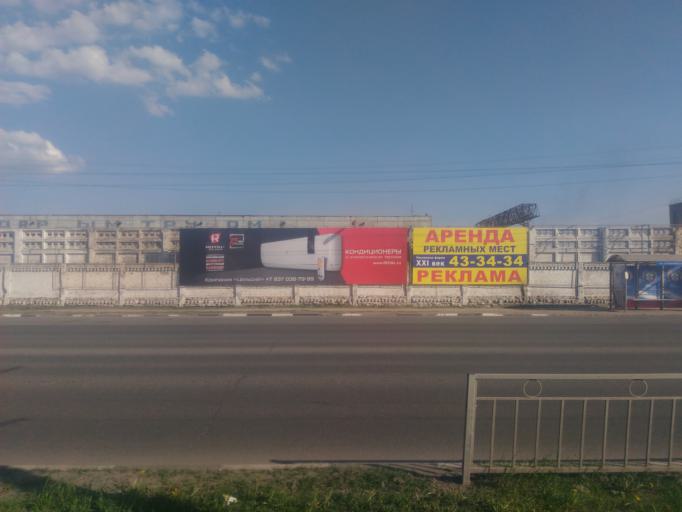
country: RU
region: Ulyanovsk
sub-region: Ulyanovskiy Rayon
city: Ulyanovsk
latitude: 54.2812
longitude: 48.3479
